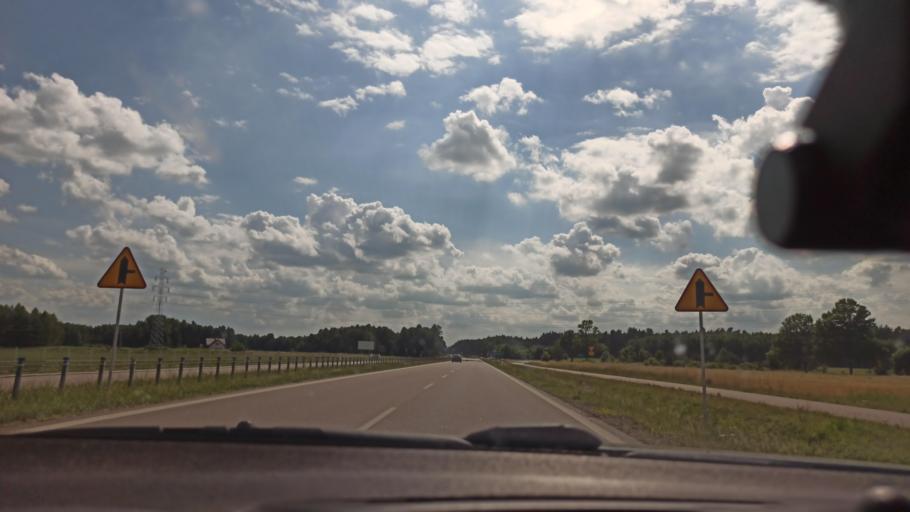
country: PL
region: Podlasie
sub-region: Powiat bialostocki
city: Turosn Koscielna
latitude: 53.0419
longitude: 23.0287
